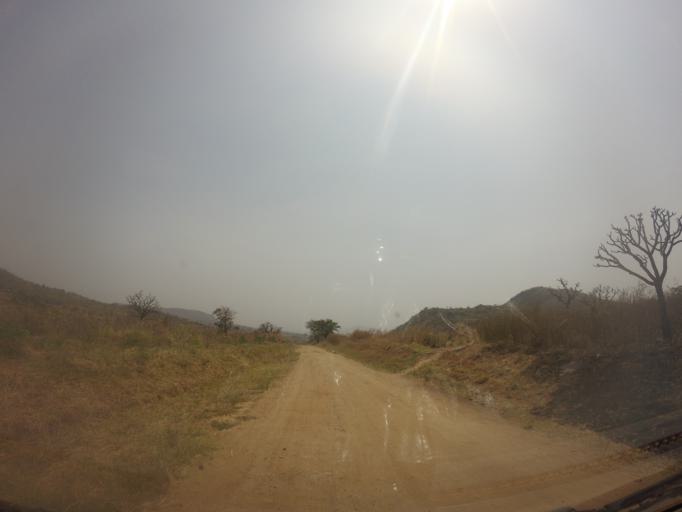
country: UG
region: Northern Region
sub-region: Arua District
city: Arua
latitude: 2.9250
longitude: 30.9848
